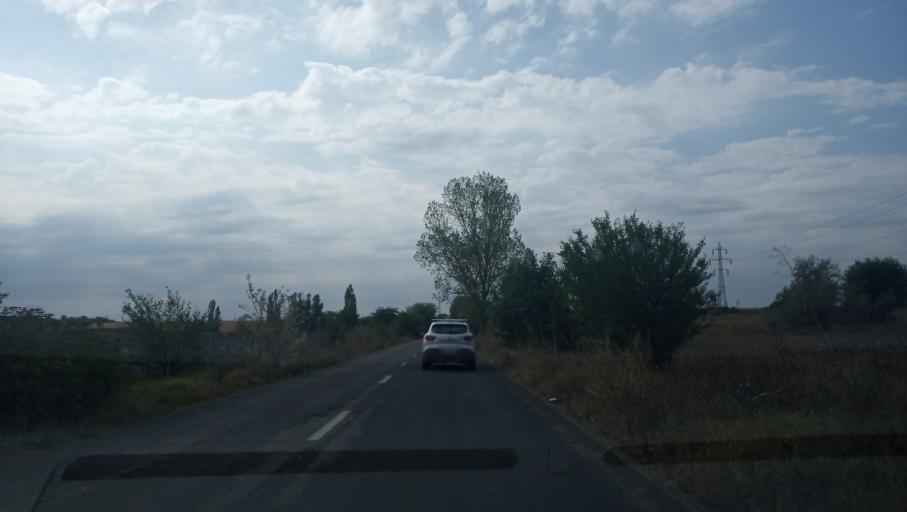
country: RO
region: Constanta
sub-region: Comuna Limanu
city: Limanu
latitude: 43.8181
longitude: 28.5498
